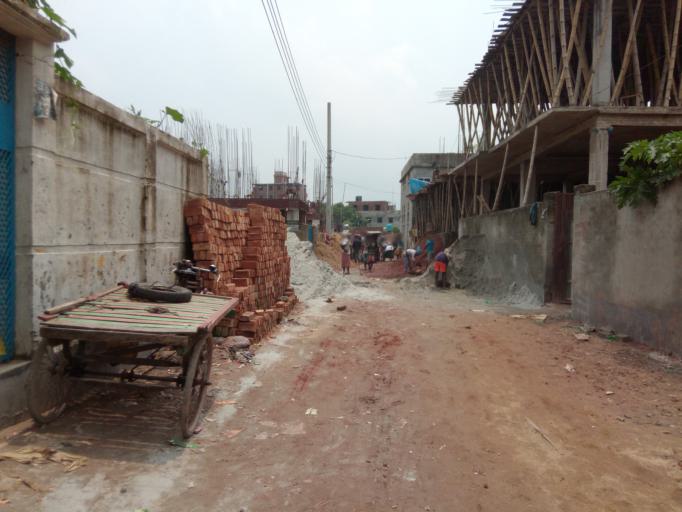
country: BD
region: Dhaka
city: Azimpur
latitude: 23.7553
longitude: 90.3516
